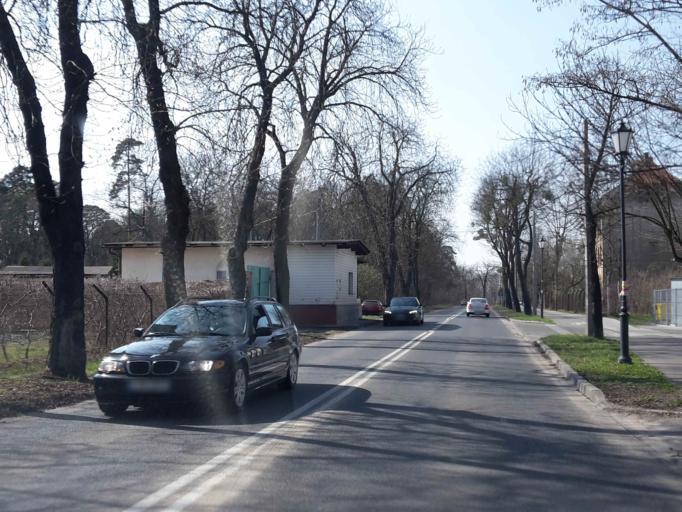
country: PL
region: Kujawsko-Pomorskie
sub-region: Torun
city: Torun
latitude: 53.0118
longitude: 18.5643
